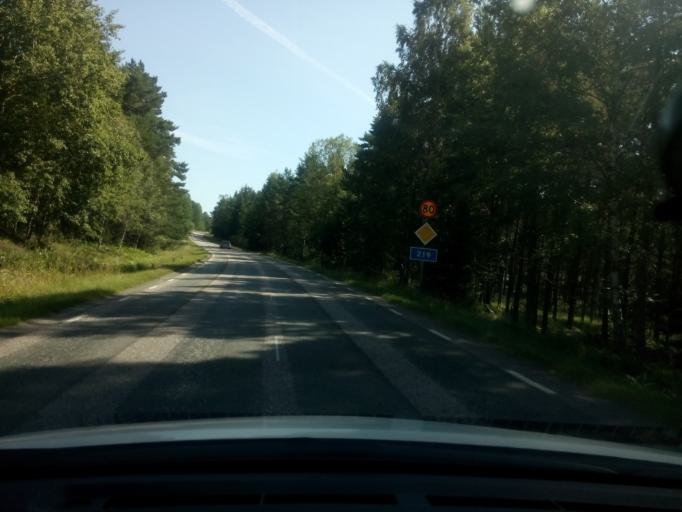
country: SE
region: Soedermanland
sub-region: Oxelosunds Kommun
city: Oxelosund
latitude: 58.7386
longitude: 17.2388
